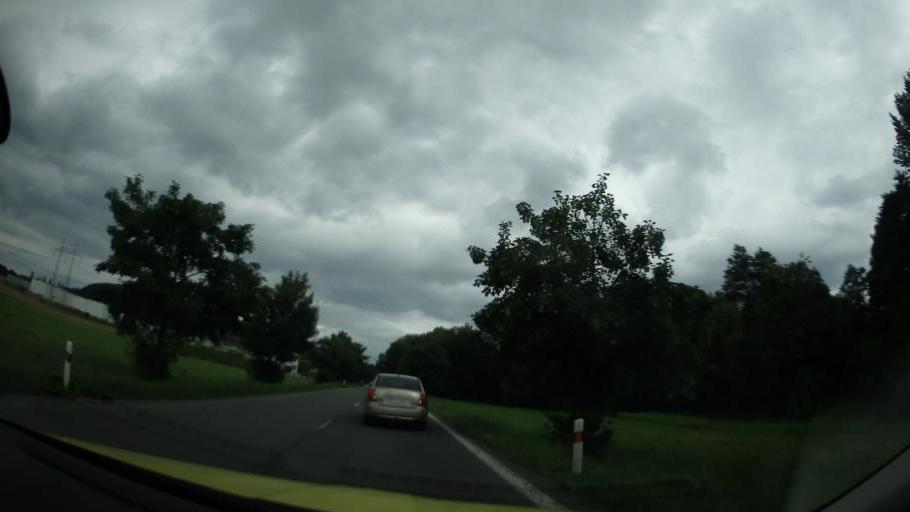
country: CZ
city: Verovice
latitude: 49.5415
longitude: 18.0907
